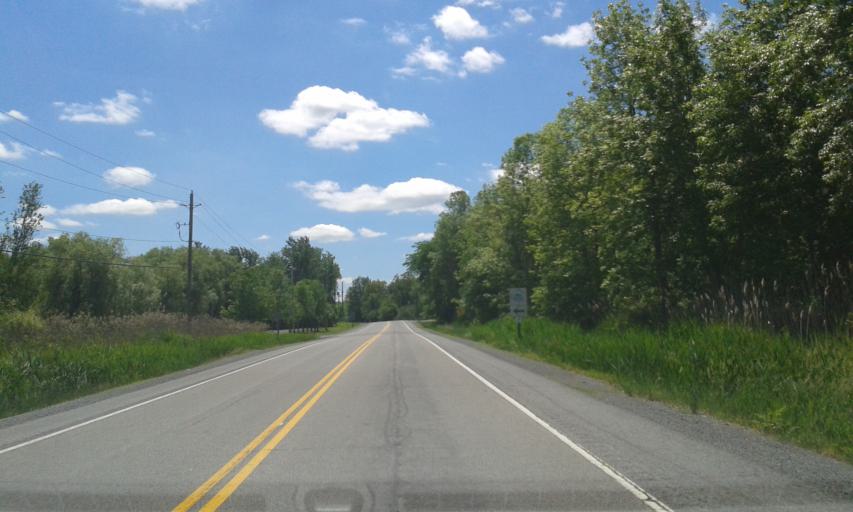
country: CA
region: Ontario
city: Cornwall
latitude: 45.1177
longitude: -74.5172
